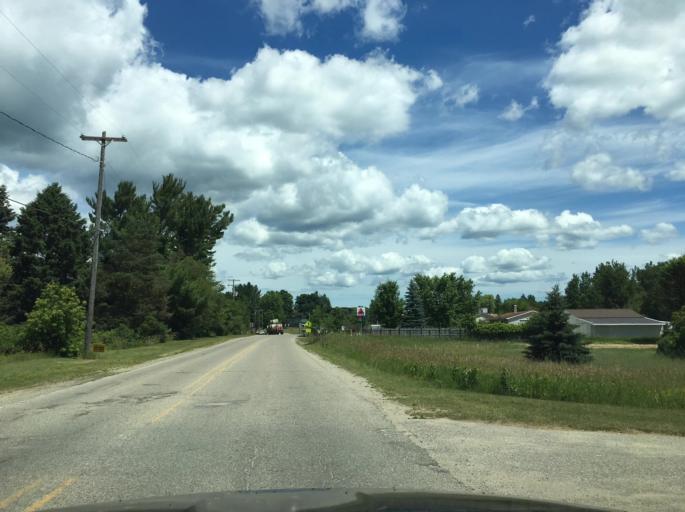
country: US
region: Michigan
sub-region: Osceola County
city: Reed City
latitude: 43.8554
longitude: -85.4443
